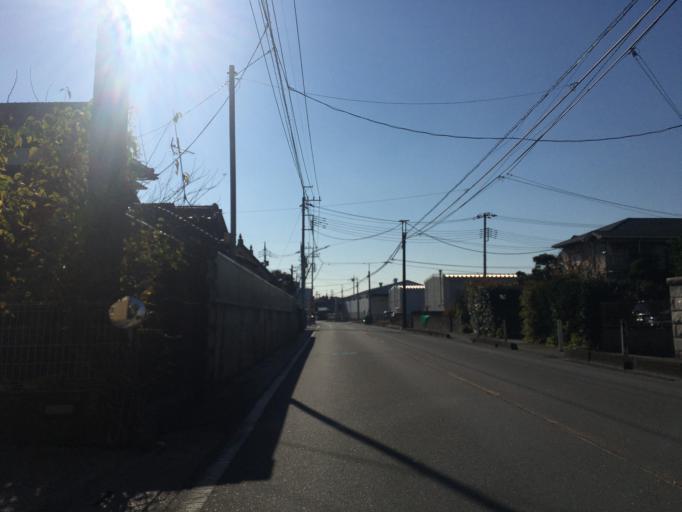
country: JP
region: Saitama
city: Soka
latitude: 35.8009
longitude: 139.8220
